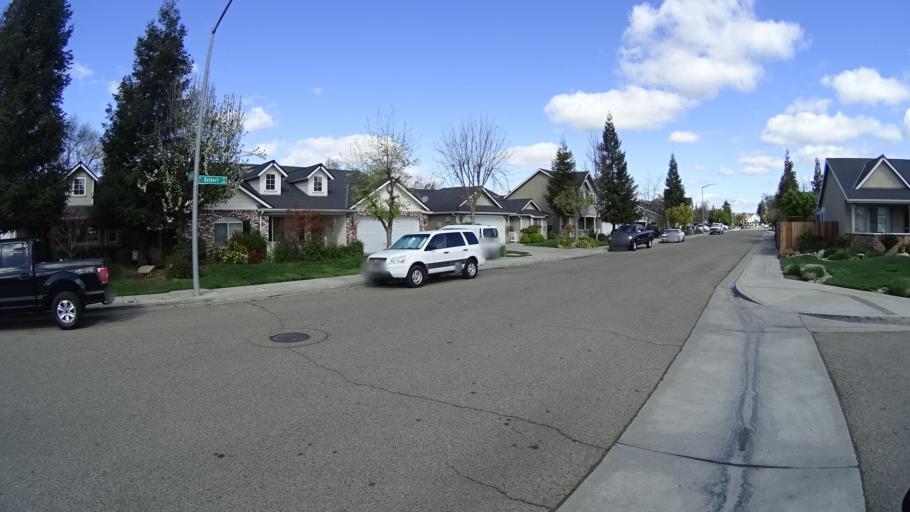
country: US
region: California
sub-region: Fresno County
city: West Park
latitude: 36.8339
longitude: -119.8878
